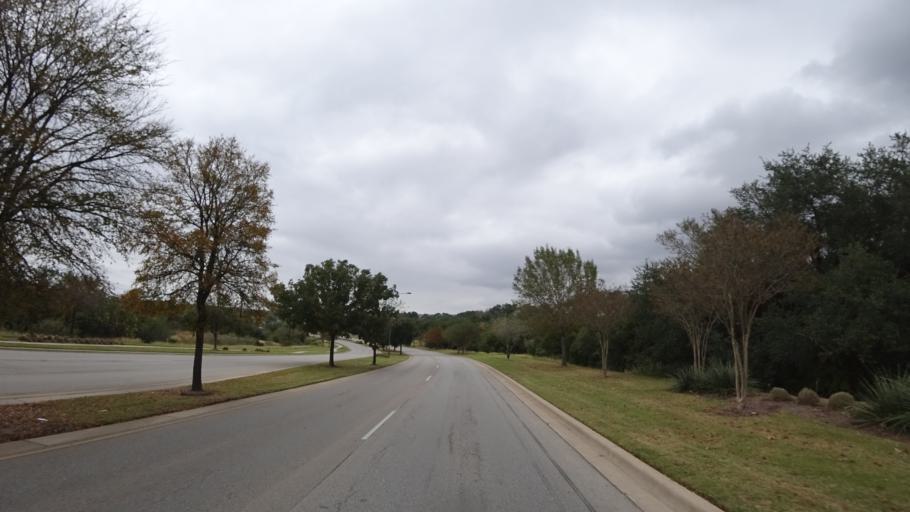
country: US
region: Texas
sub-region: Travis County
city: Hudson Bend
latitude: 30.3746
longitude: -97.8854
